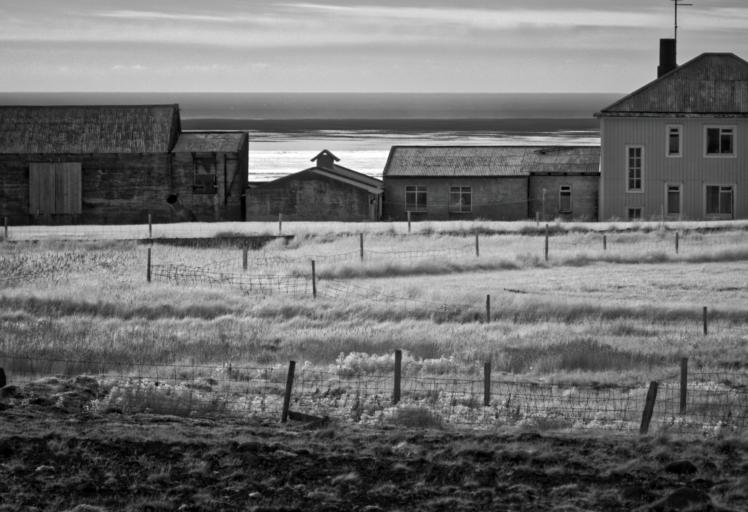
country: IS
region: East
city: Hoefn
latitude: 63.8811
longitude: -16.6443
